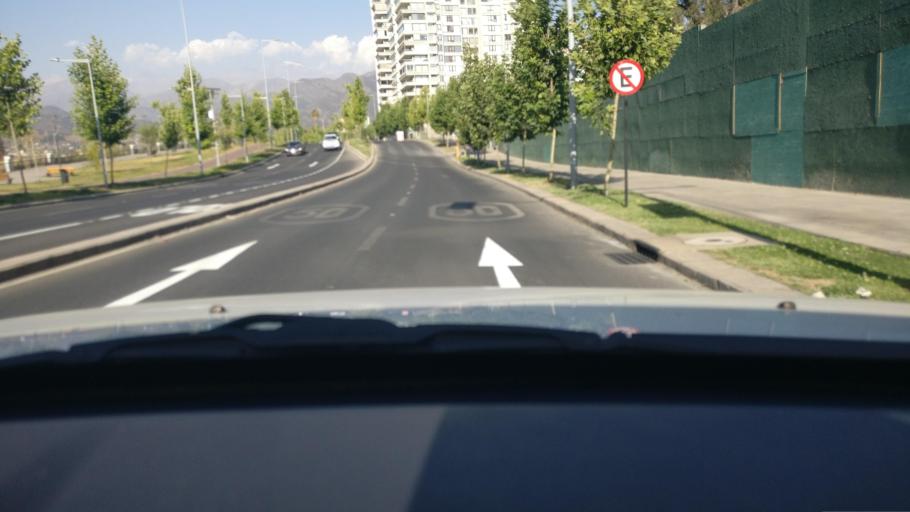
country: CL
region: Santiago Metropolitan
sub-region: Provincia de Santiago
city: Villa Presidente Frei, Nunoa, Santiago, Chile
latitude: -33.3722
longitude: -70.5219
